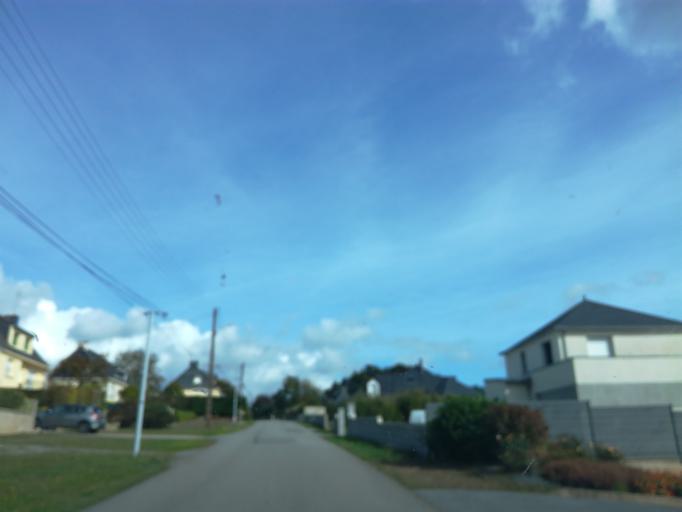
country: FR
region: Brittany
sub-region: Departement du Morbihan
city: Rohan
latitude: 48.0664
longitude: -2.7619
